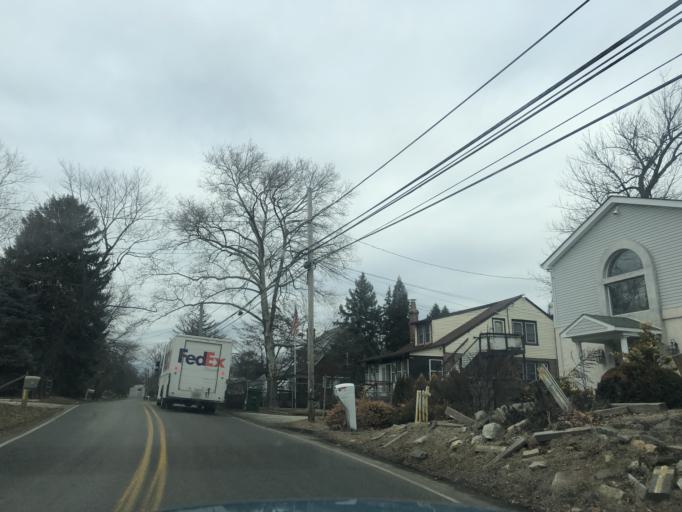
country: US
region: Pennsylvania
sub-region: Montgomery County
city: Bridgeport
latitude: 40.0950
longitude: -75.3487
